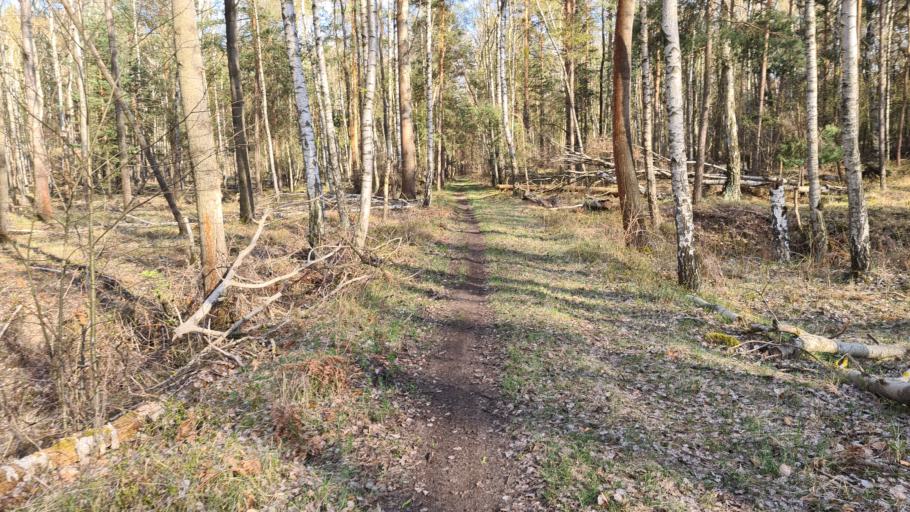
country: DE
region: Brandenburg
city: Trobitz
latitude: 51.5942
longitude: 13.4531
